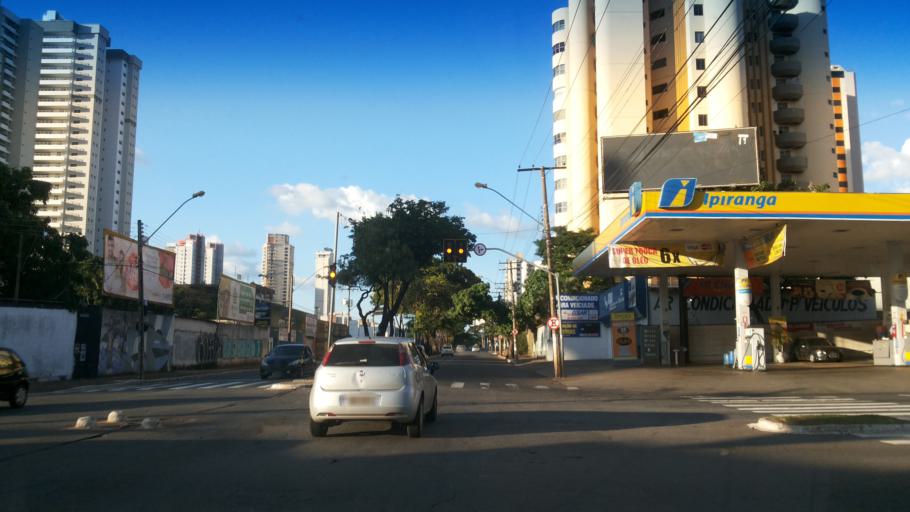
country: BR
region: Goias
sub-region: Goiania
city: Goiania
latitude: -16.7012
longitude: -49.2711
